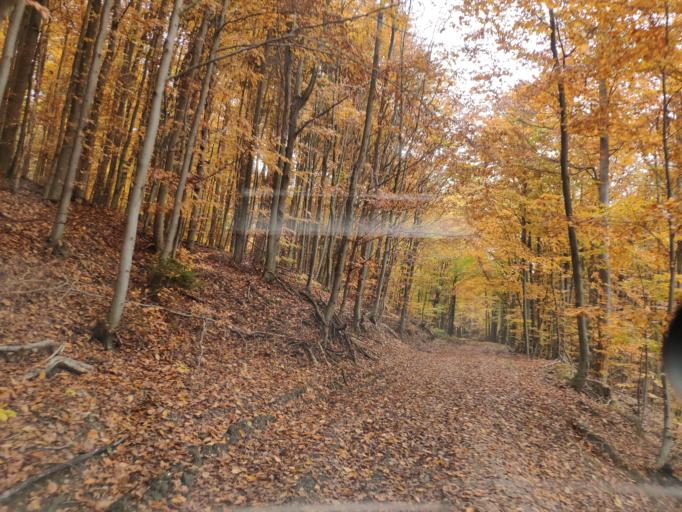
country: SK
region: Kosicky
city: Moldava nad Bodvou
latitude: 48.7332
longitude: 21.0257
